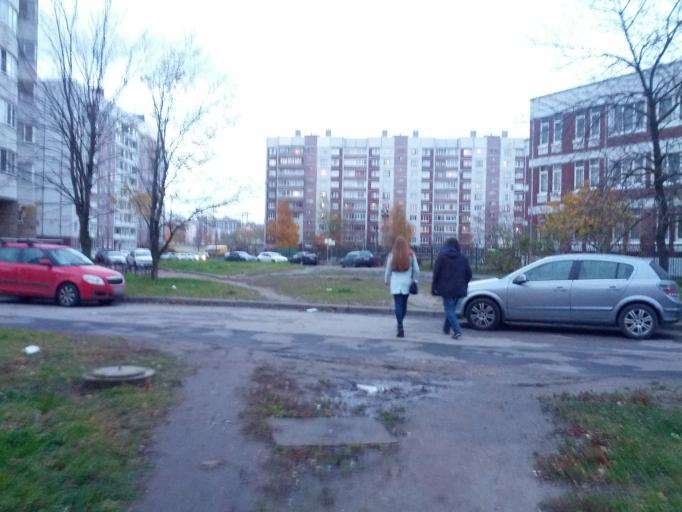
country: RU
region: Leningrad
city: Rybatskoye
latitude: 59.8989
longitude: 30.4923
